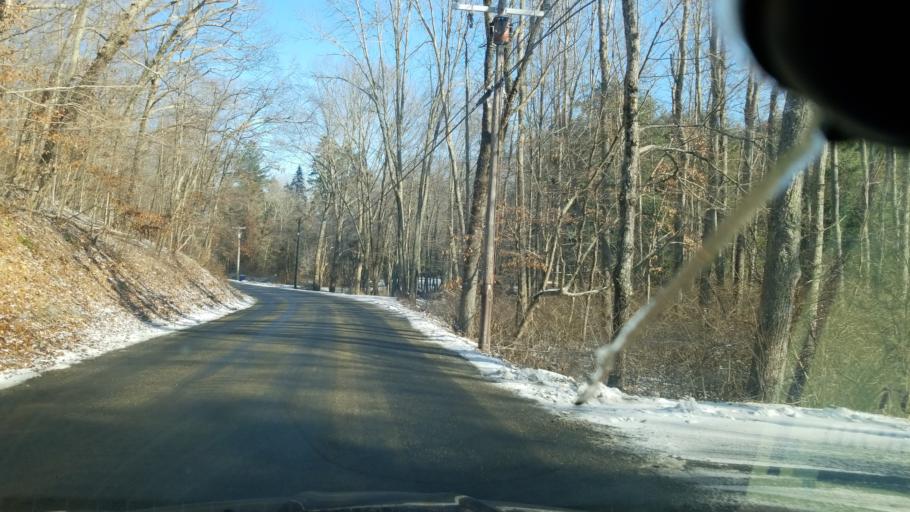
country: US
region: Connecticut
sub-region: Windham County
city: East Brooklyn
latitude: 41.8400
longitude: -71.9339
